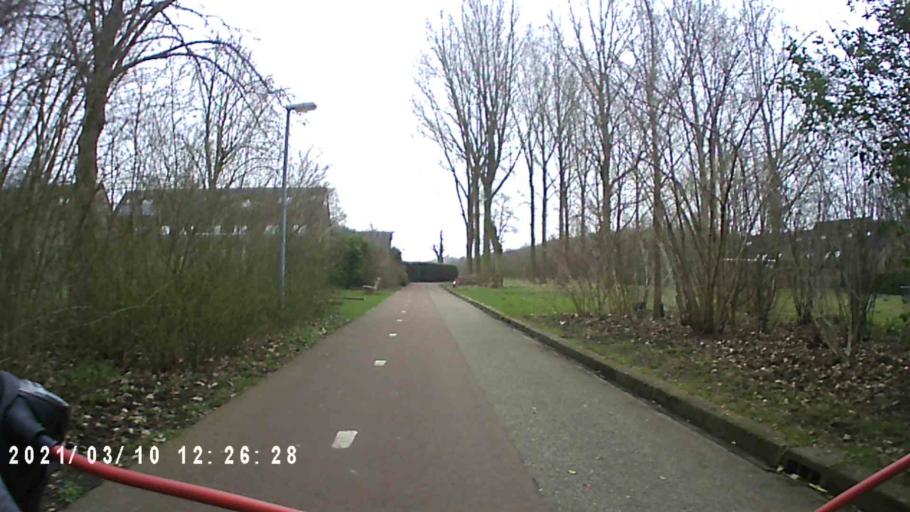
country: NL
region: Groningen
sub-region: Gemeente Groningen
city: Oosterpark
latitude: 53.2510
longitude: 6.6048
